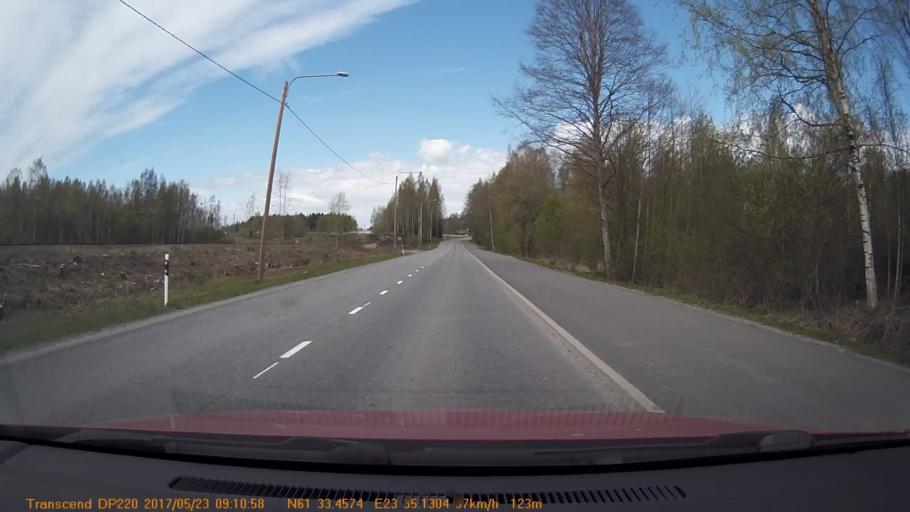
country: FI
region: Pirkanmaa
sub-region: Tampere
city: Yloejaervi
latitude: 61.5575
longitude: 23.5858
